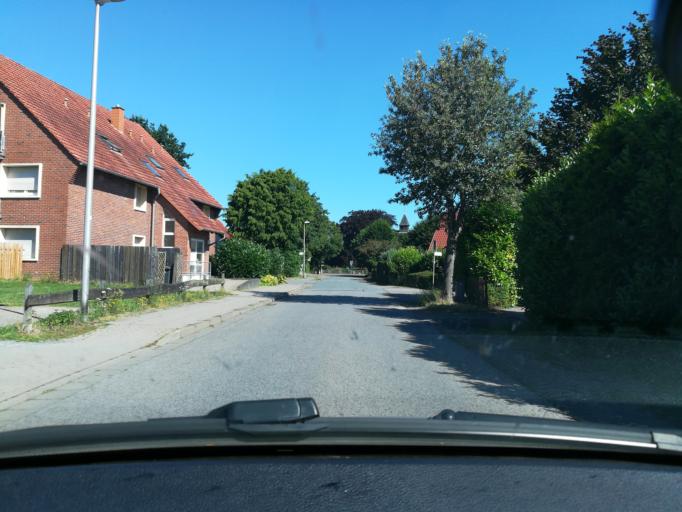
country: DE
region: North Rhine-Westphalia
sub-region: Regierungsbezirk Detmold
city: Minden
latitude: 52.3164
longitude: 8.9315
